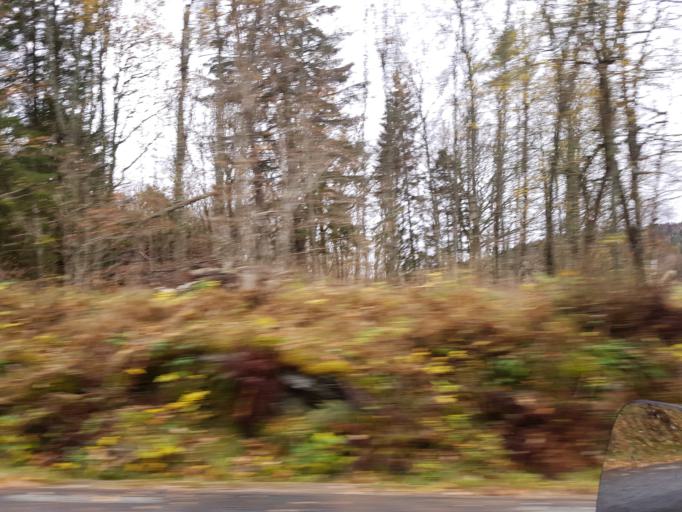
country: SE
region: Vaestra Goetaland
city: Svanesund
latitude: 58.2425
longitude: 11.8038
